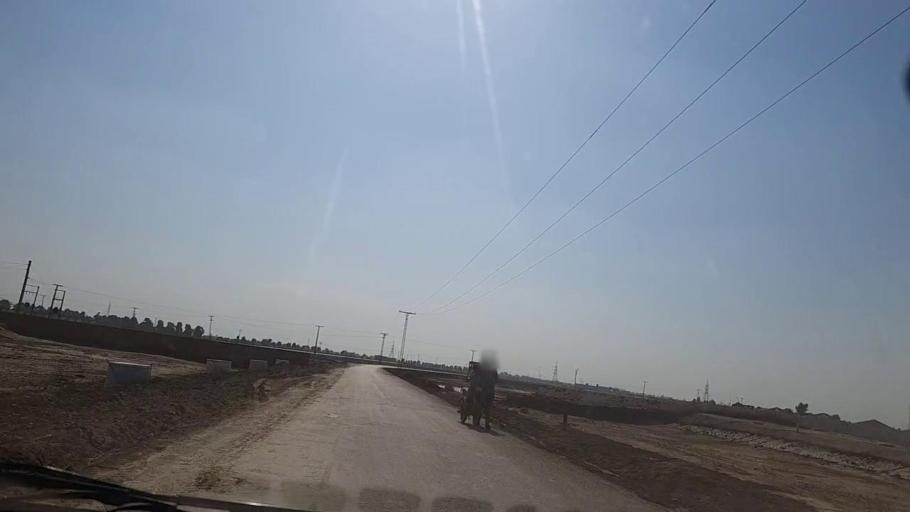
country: PK
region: Sindh
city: Mirpur Khas
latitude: 25.5177
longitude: 68.9531
